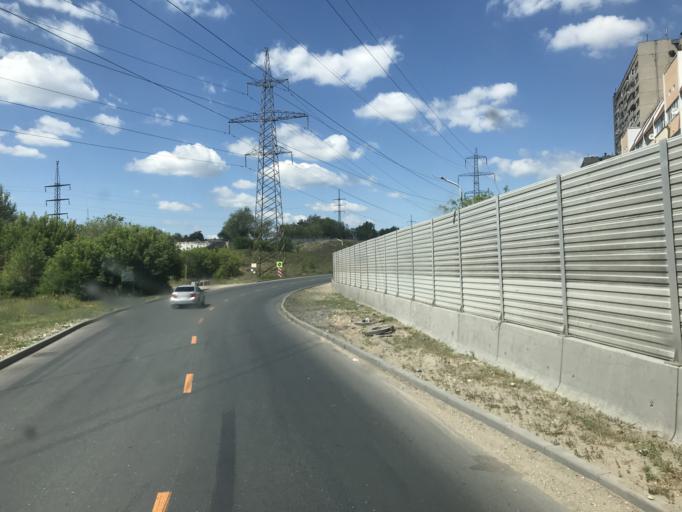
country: RU
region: Samara
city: Zhigulevsk
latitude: 53.4716
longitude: 49.5126
